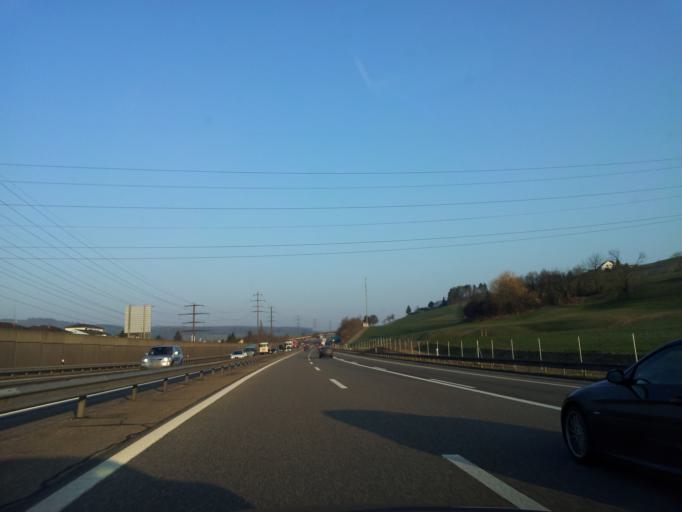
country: CH
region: Aargau
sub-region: Bezirk Laufenburg
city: Frick
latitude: 47.5039
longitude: 8.0342
